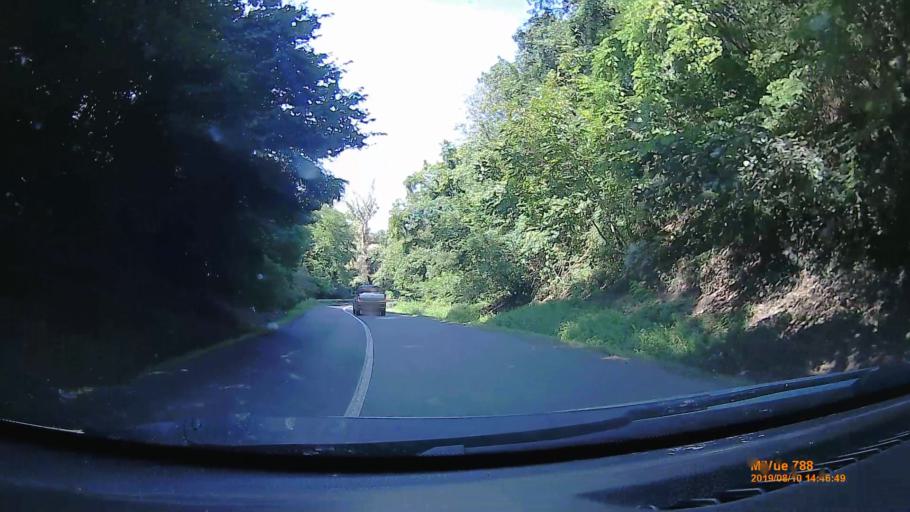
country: HU
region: Somogy
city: Somogyvar
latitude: 46.5938
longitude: 17.6434
